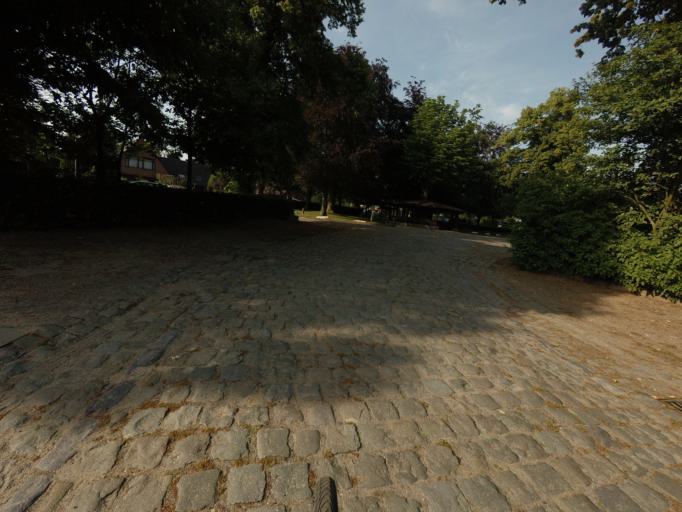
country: BE
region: Flanders
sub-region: Provincie Antwerpen
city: Zandhoven
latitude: 51.1989
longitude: 4.6353
